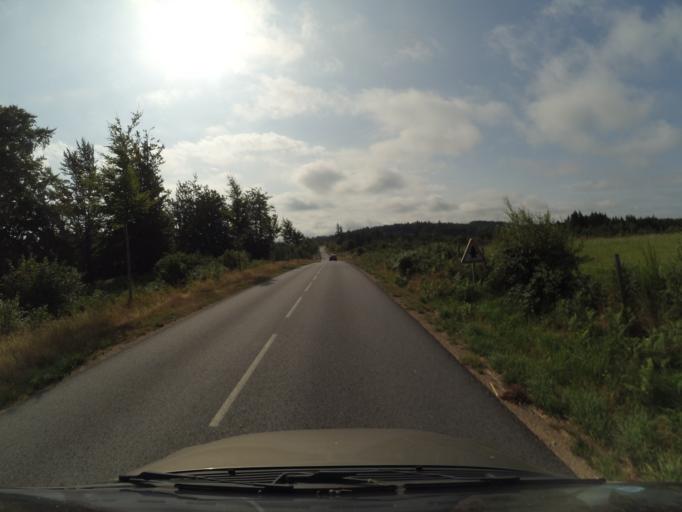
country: FR
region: Limousin
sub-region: Departement de la Correze
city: Meymac
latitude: 45.6051
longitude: 2.1133
